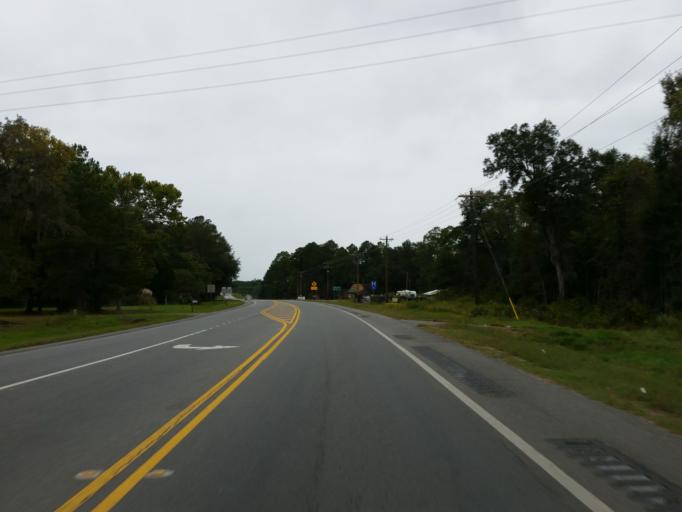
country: US
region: Georgia
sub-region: Lanier County
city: Lakeland
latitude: 31.0479
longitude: -83.0325
